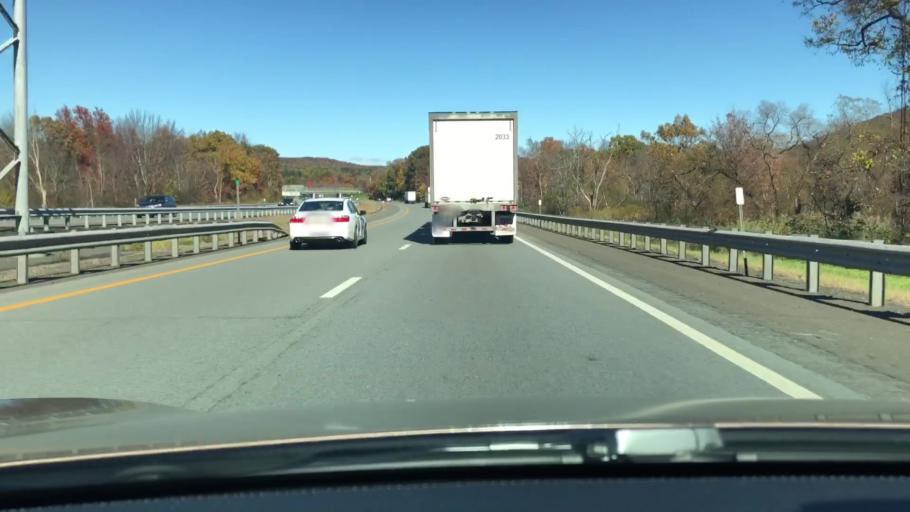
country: US
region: New York
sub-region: Orange County
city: Central Valley
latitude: 41.3207
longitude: -74.1132
